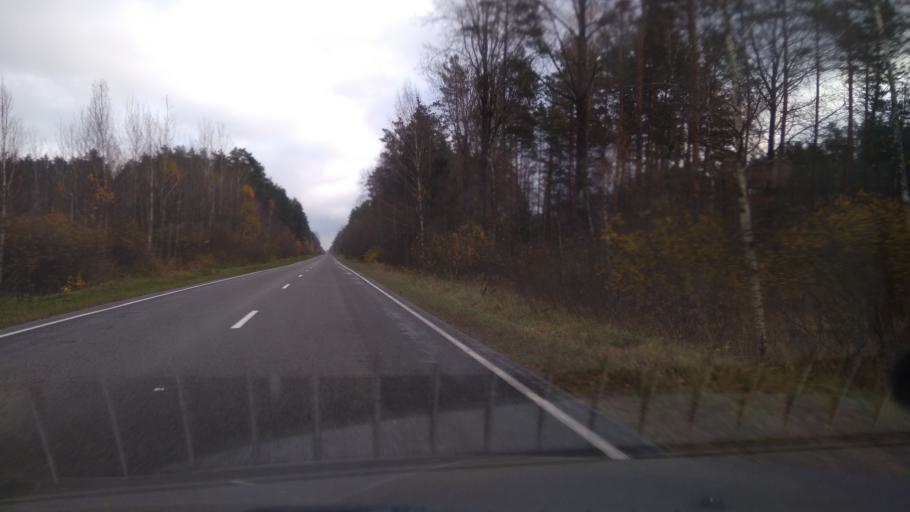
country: BY
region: Minsk
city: Urechcha
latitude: 53.2090
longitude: 27.9567
